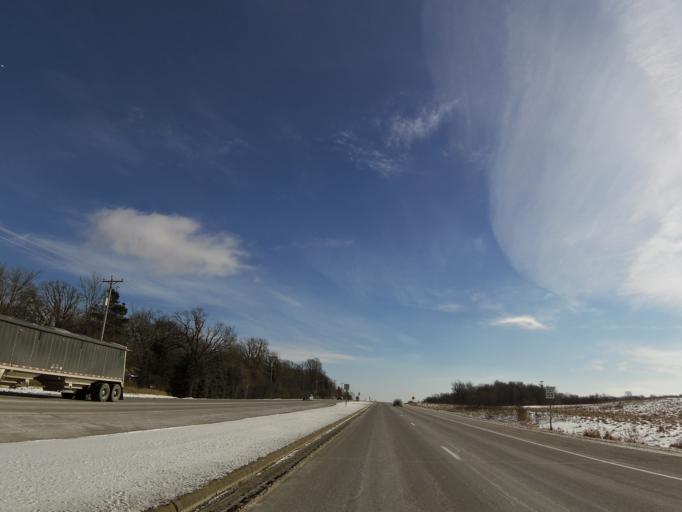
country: US
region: Minnesota
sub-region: Dakota County
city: Rosemount
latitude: 44.7389
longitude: -93.0545
